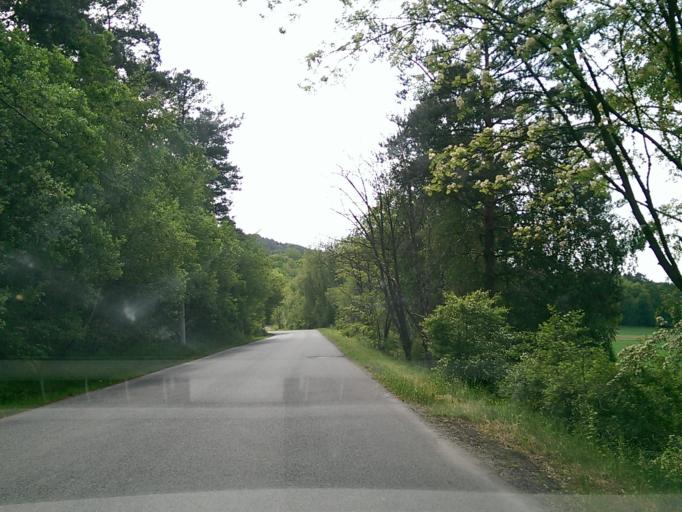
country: CZ
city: Ohrazenice
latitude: 50.5635
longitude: 15.1212
